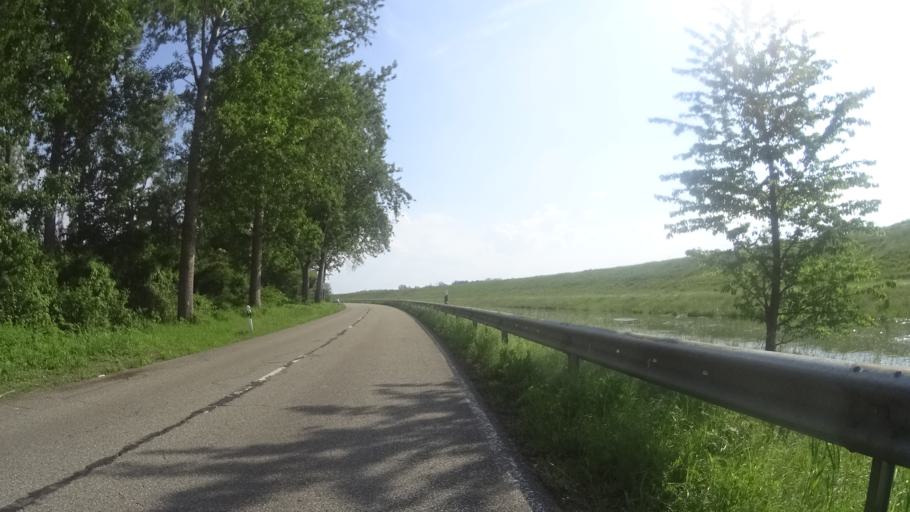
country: DE
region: Baden-Wuerttemberg
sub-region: Karlsruhe Region
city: Schwarzach
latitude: 48.7840
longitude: 8.0296
